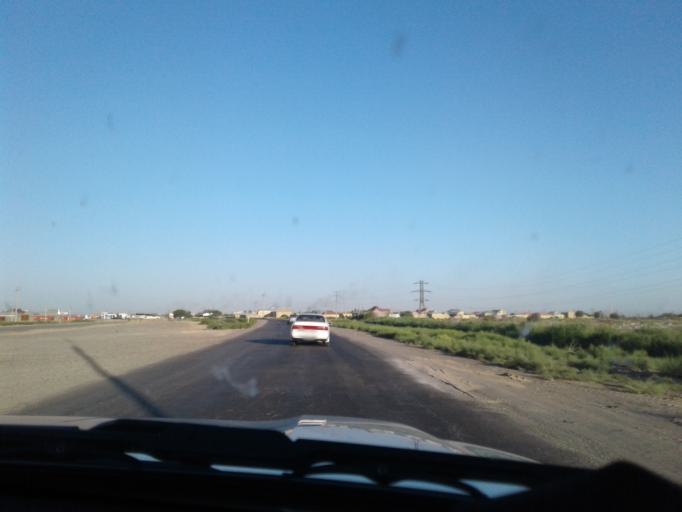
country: TM
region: Mary
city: Mary
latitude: 37.5683
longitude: 61.8090
